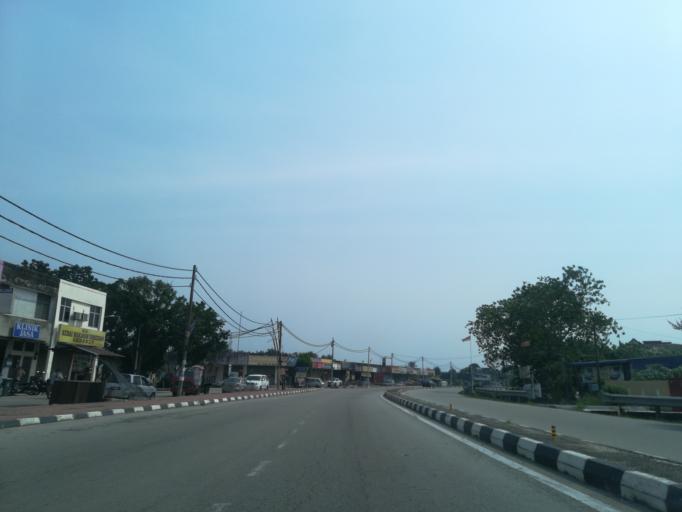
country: MY
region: Kedah
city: Kulim
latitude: 5.4205
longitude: 100.5499
